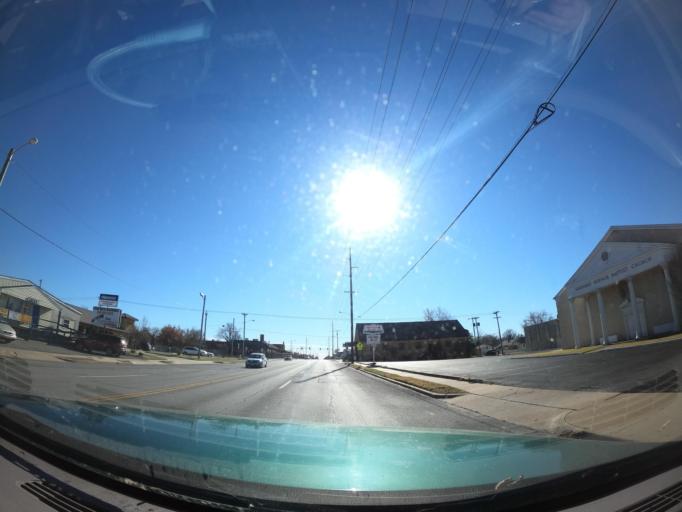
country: US
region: Oklahoma
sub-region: Tulsa County
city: Tulsa
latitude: 36.1376
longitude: -95.9404
